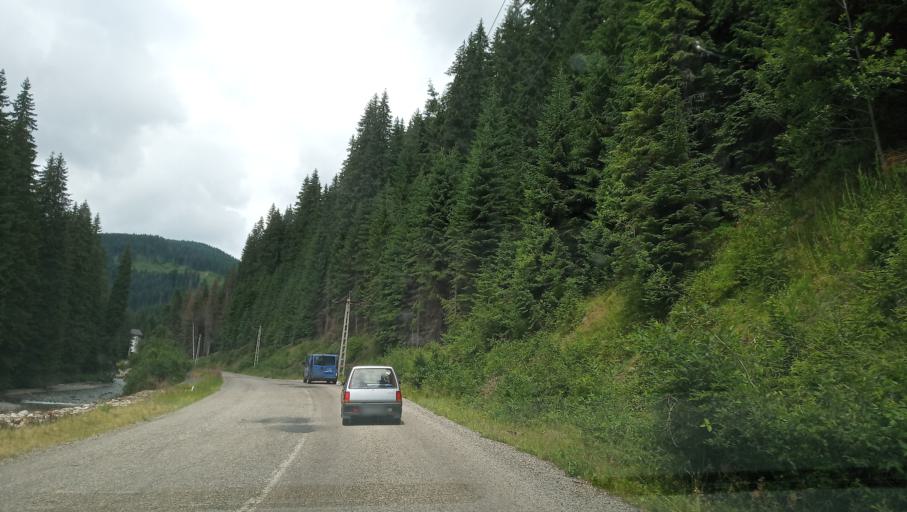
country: RO
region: Hunedoara
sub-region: Oras Petrila
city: Petrila
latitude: 45.4339
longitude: 23.6406
